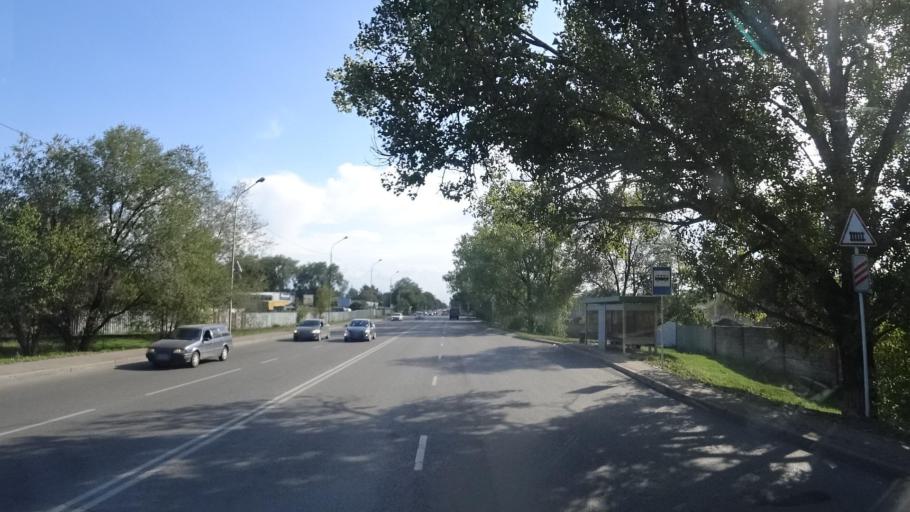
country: KZ
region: Almaty Oblysy
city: Energeticheskiy
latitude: 43.3784
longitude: 76.9961
